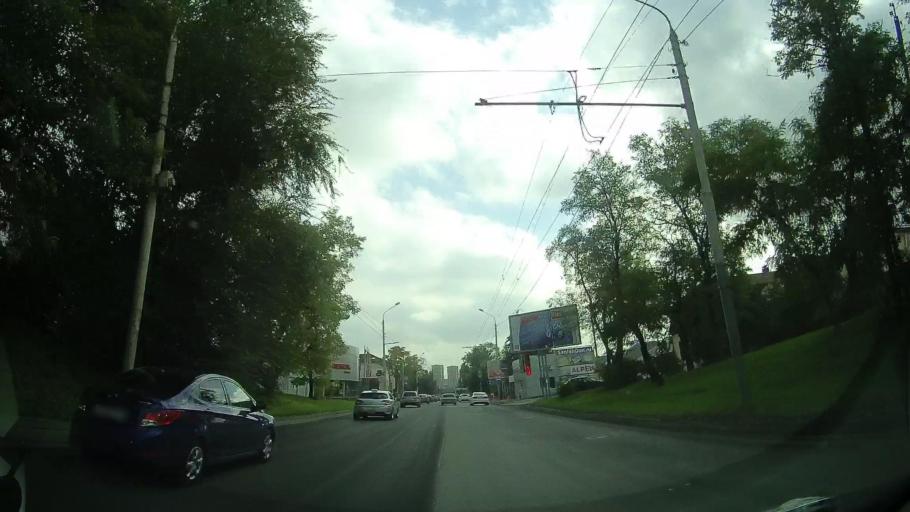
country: RU
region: Rostov
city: Rostov-na-Donu
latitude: 47.2540
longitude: 39.6938
